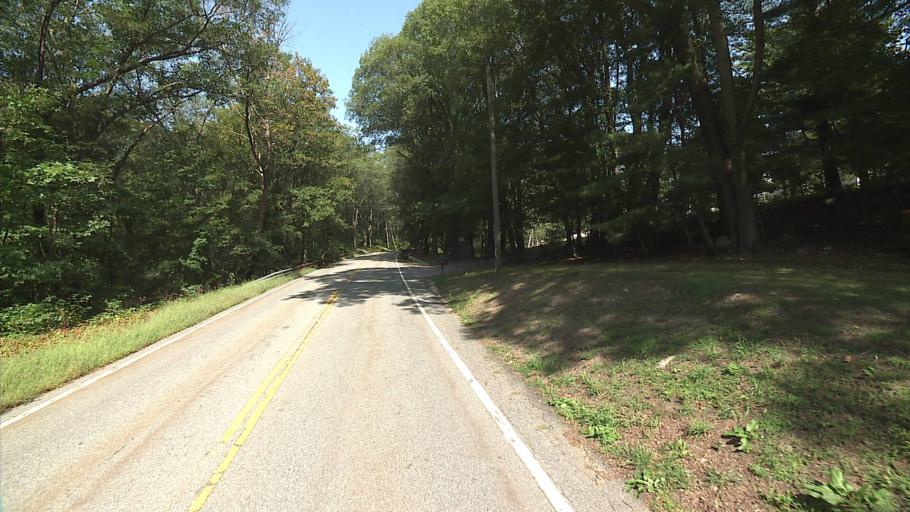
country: US
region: Connecticut
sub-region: Windham County
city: Quinebaug
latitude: 42.0196
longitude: -72.0081
